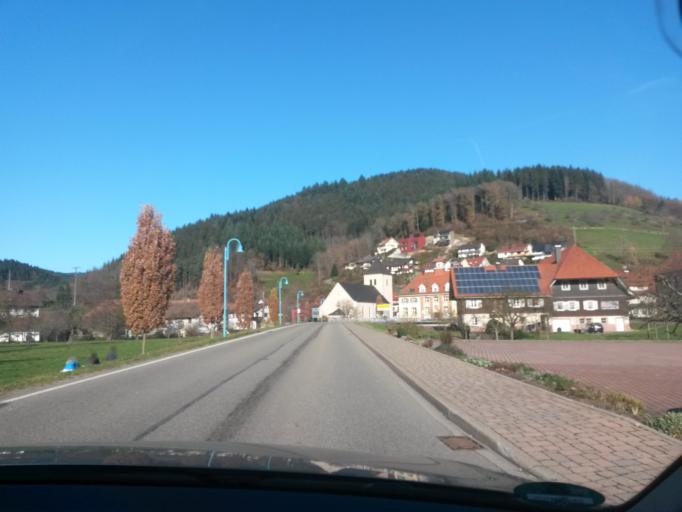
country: DE
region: Baden-Wuerttemberg
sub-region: Freiburg Region
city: Oberwolfach
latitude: 48.3431
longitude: 8.2250
